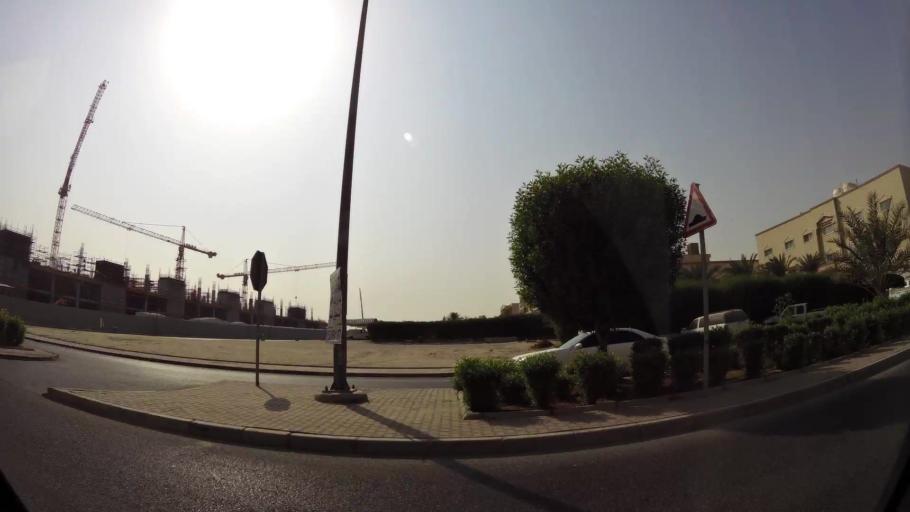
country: KW
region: Al Asimah
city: Ar Rabiyah
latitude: 29.2735
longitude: 47.9010
